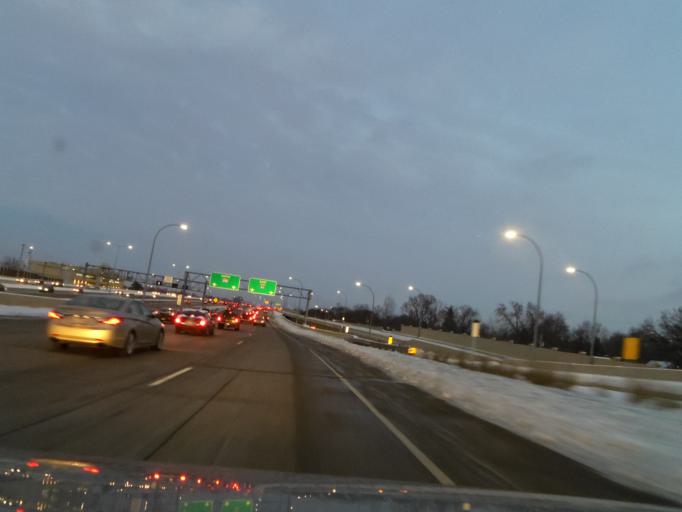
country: US
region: Minnesota
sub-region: Hennepin County
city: Richfield
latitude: 44.8897
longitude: -93.2928
